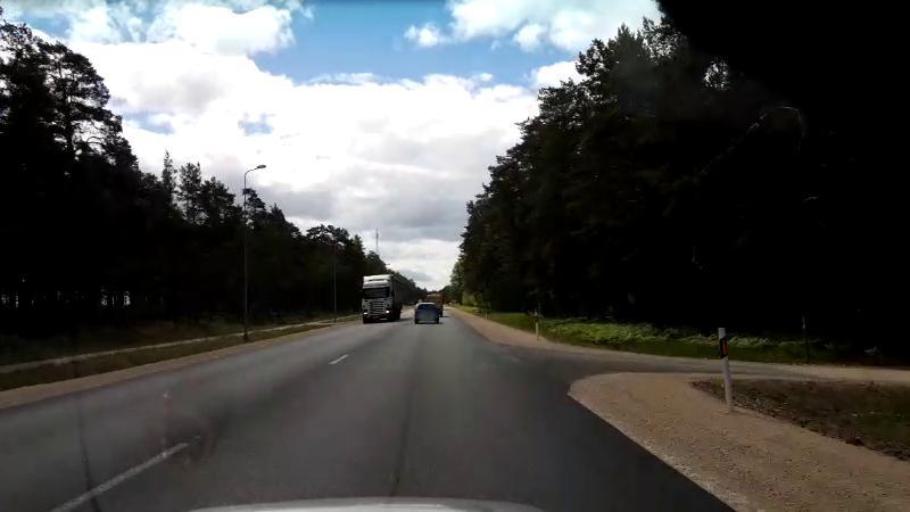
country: LV
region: Salacgrivas
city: Salacgriva
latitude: 57.7692
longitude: 24.3558
